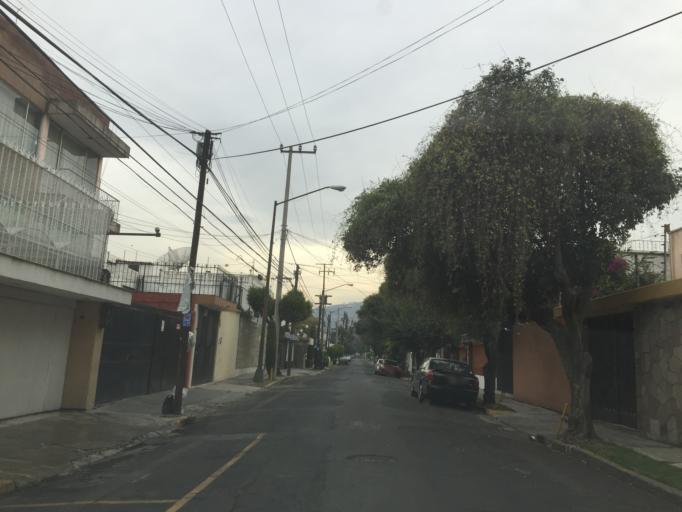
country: MX
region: Mexico
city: Colonia Lindavista
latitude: 19.4914
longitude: -99.1319
